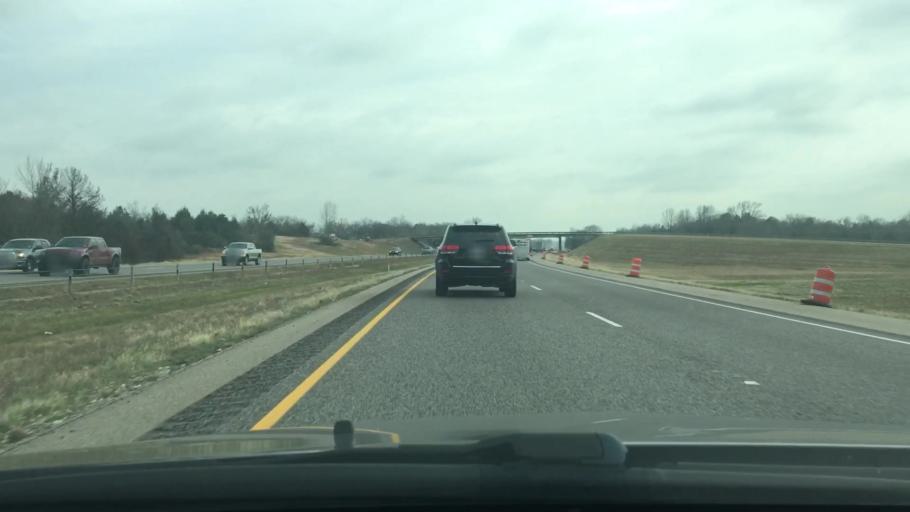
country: US
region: Texas
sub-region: Leon County
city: Buffalo
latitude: 31.5026
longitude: -96.0982
